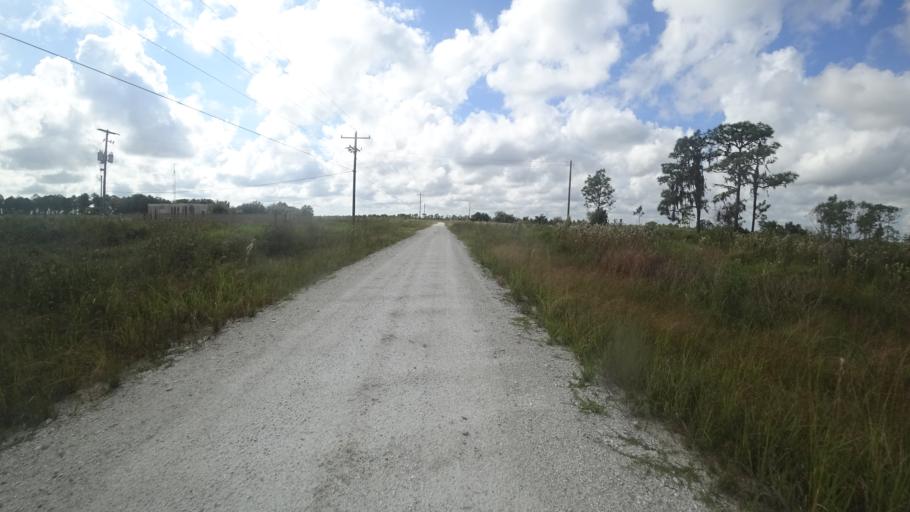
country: US
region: Florida
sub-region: Hillsborough County
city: Wimauma
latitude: 27.5378
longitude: -82.1295
